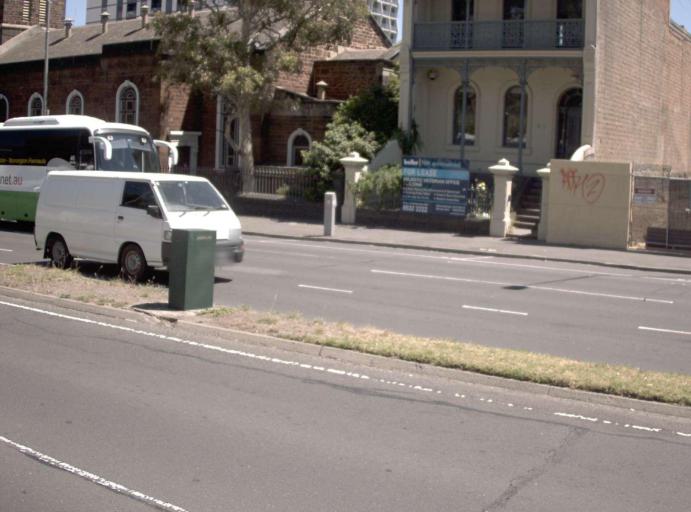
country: AU
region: Victoria
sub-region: Melbourne
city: West Melbourne
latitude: -37.8096
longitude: 144.9527
